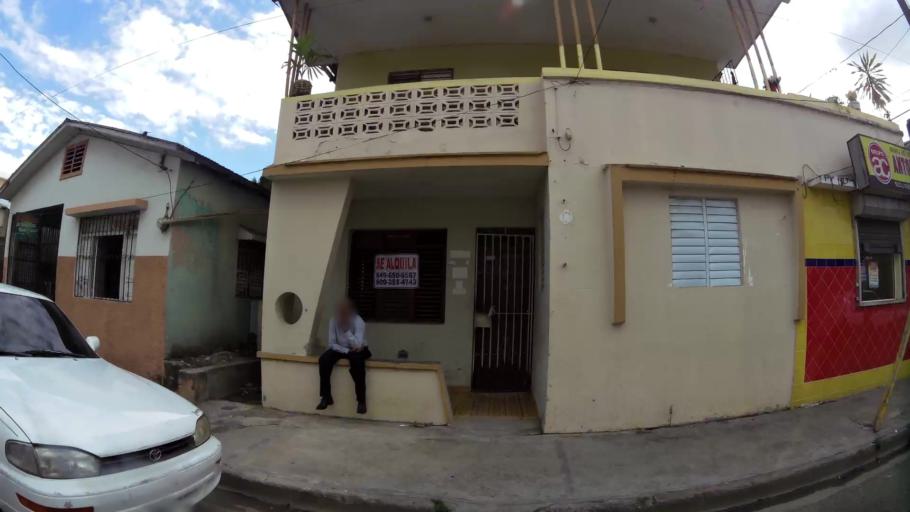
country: DO
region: La Vega
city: Concepcion de La Vega
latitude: 19.2277
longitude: -70.5331
